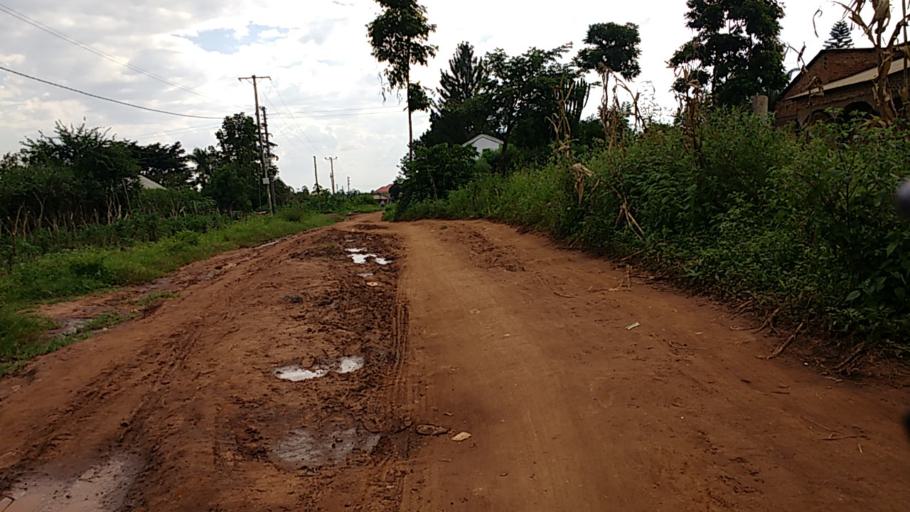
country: UG
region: Eastern Region
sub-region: Mbale District
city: Mbale
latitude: 1.0669
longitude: 34.1661
